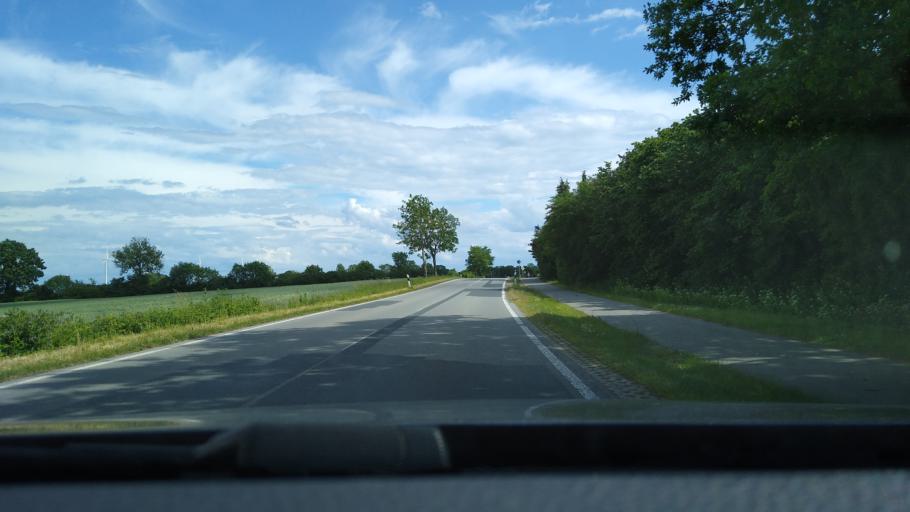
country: DE
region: Schleswig-Holstein
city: Kabelhorst
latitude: 54.2140
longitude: 10.9409
